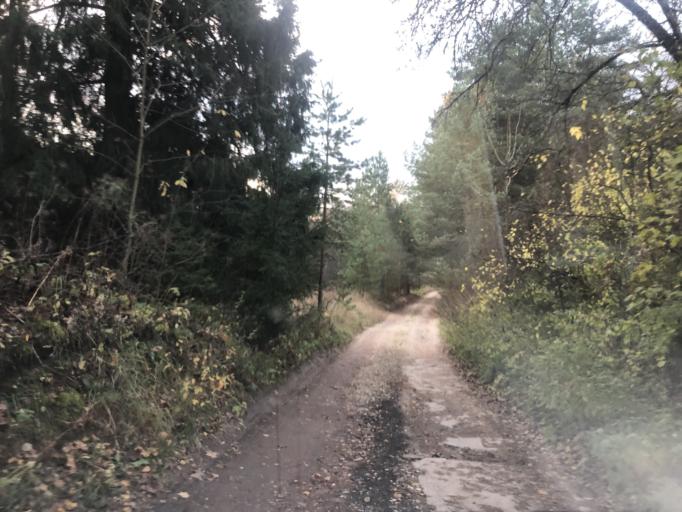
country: RU
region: Moskovskaya
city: Fryanovo
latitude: 56.1514
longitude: 38.3886
